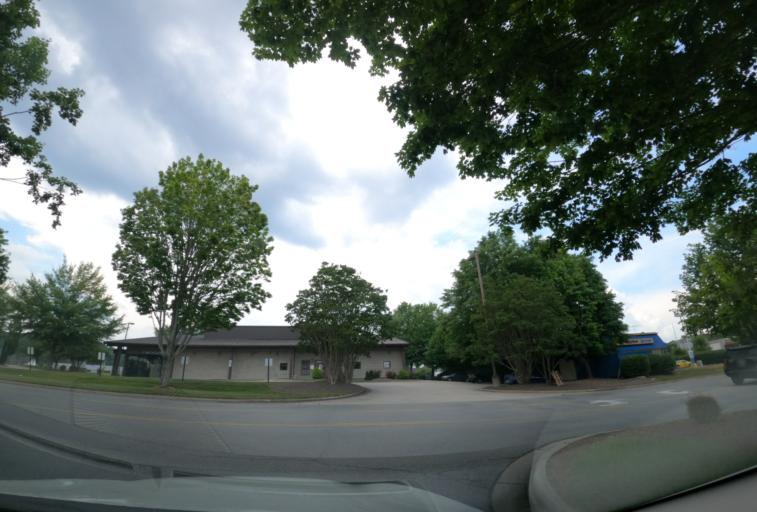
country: US
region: North Carolina
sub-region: Buncombe County
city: Bent Creek
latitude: 35.5284
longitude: -82.6053
